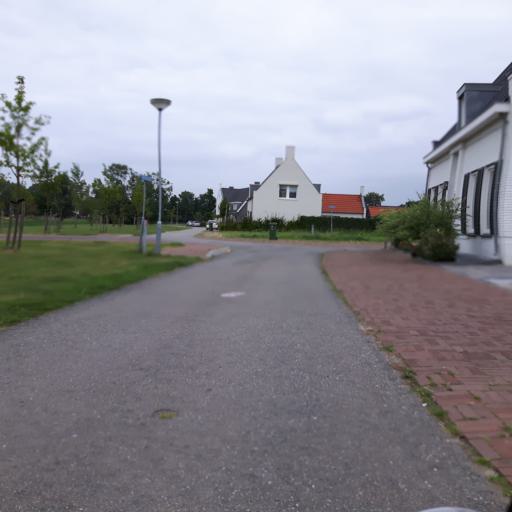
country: NL
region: Zeeland
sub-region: Gemeente Goes
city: Goes
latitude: 51.4866
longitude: 3.8954
